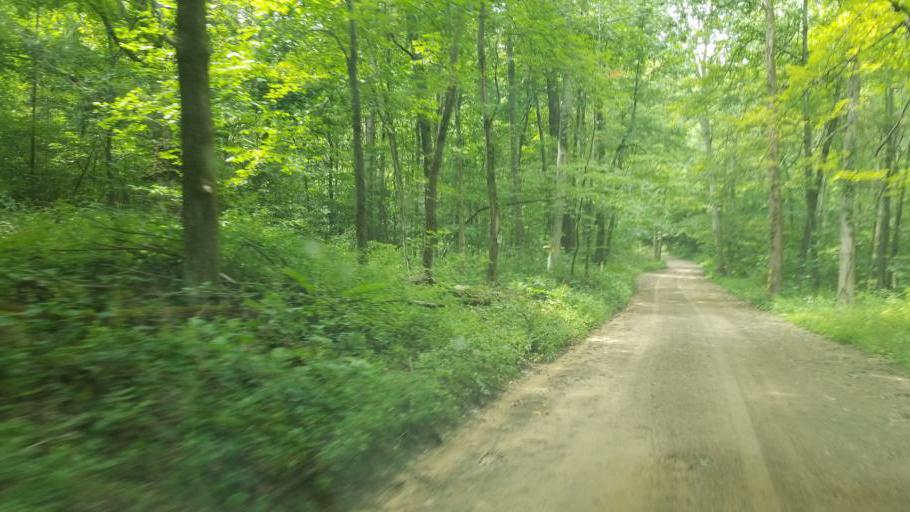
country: US
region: Ohio
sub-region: Ashland County
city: Loudonville
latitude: 40.5729
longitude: -82.2896
